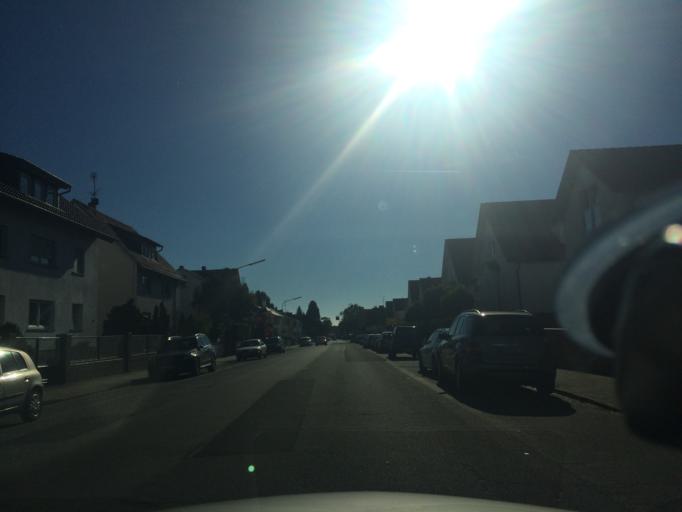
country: DE
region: Hesse
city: Morfelden-Walldorf
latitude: 49.9828
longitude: 8.5707
